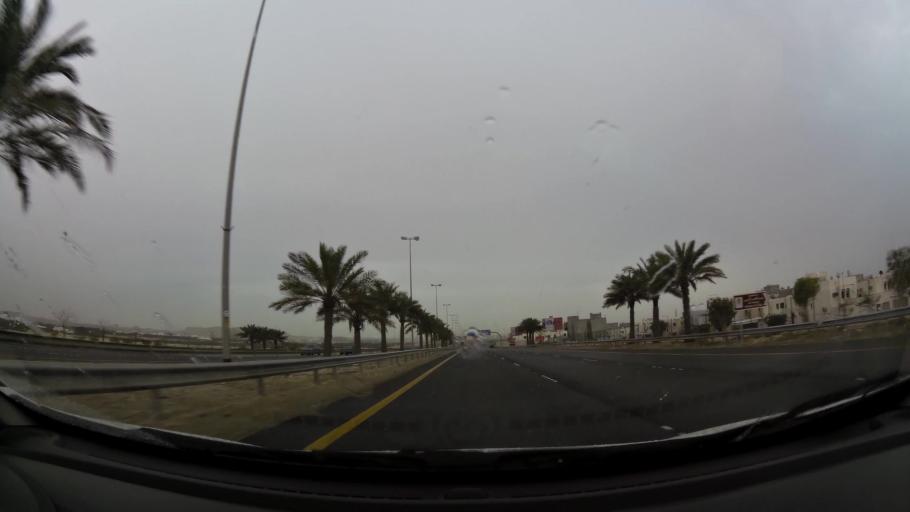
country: BH
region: Central Governorate
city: Dar Kulayb
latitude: 26.0661
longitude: 50.5162
